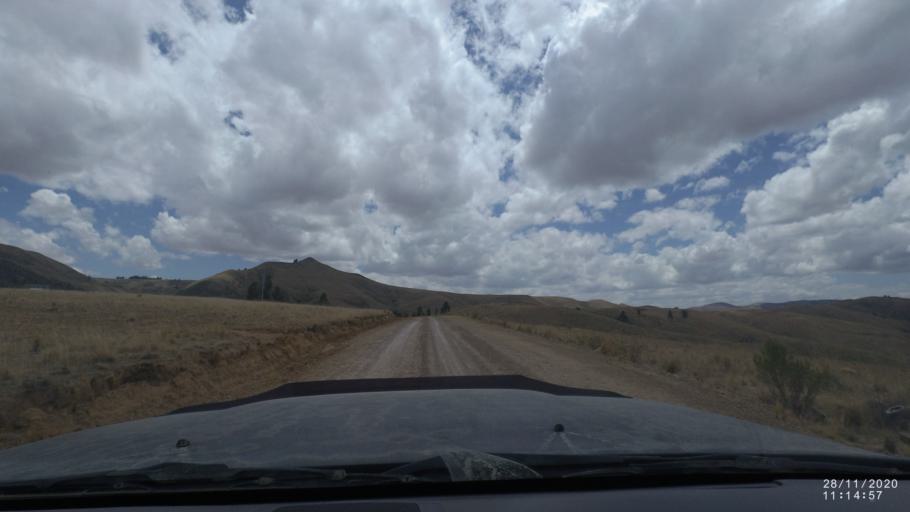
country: BO
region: Cochabamba
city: Tarata
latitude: -17.7456
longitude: -66.0934
